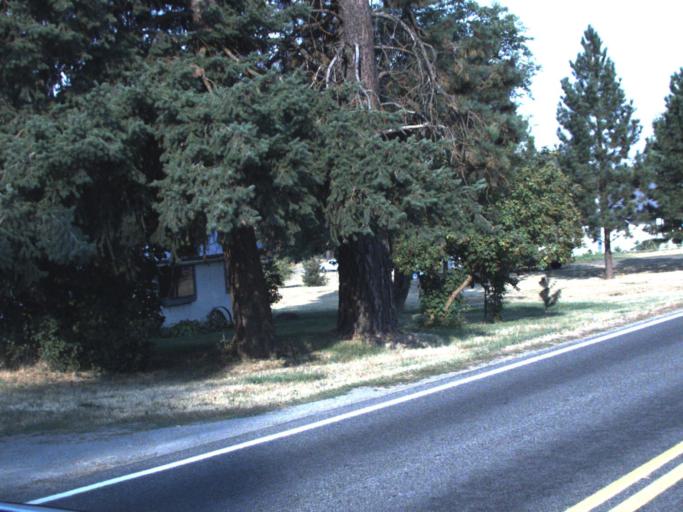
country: US
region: Washington
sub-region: Spokane County
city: Veradale
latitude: 47.4458
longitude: -117.1276
